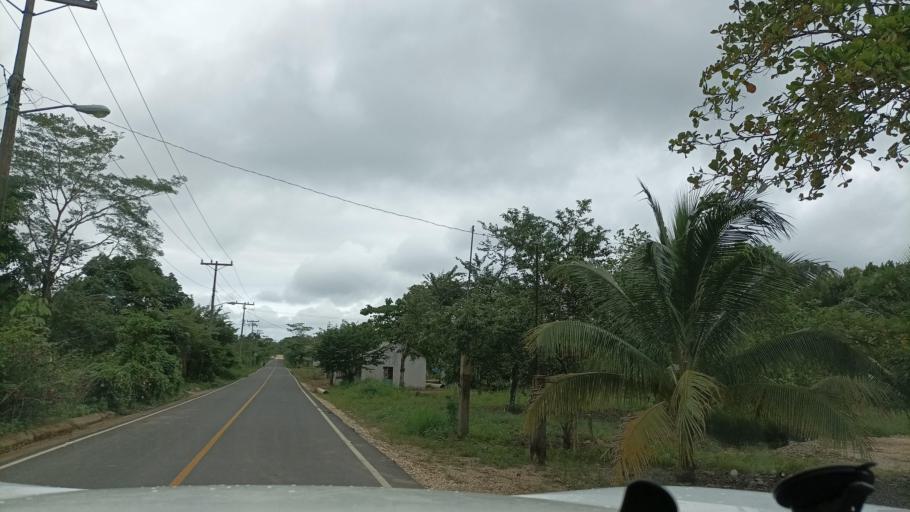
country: MX
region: Veracruz
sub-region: Moloacan
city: Cuichapa
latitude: 17.8113
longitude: -94.3556
